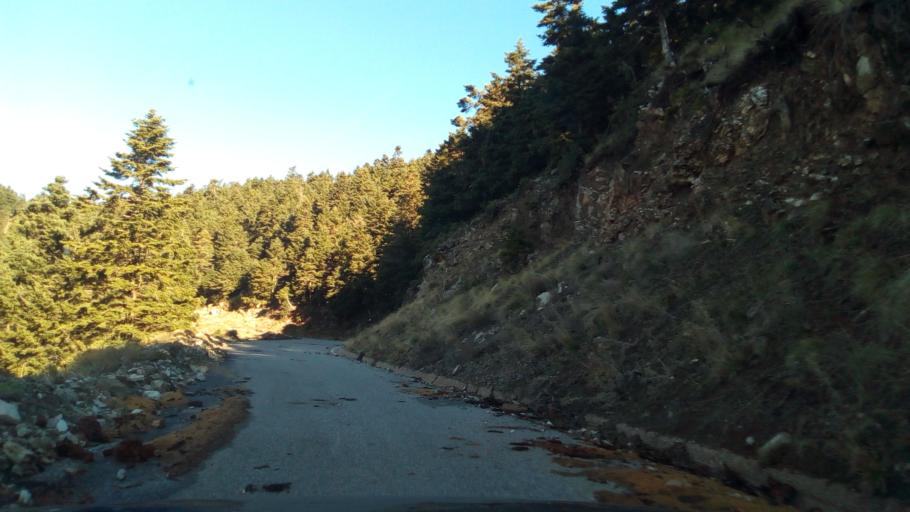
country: GR
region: West Greece
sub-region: Nomos Aitolias kai Akarnanias
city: Nafpaktos
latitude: 38.5288
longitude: 21.8481
